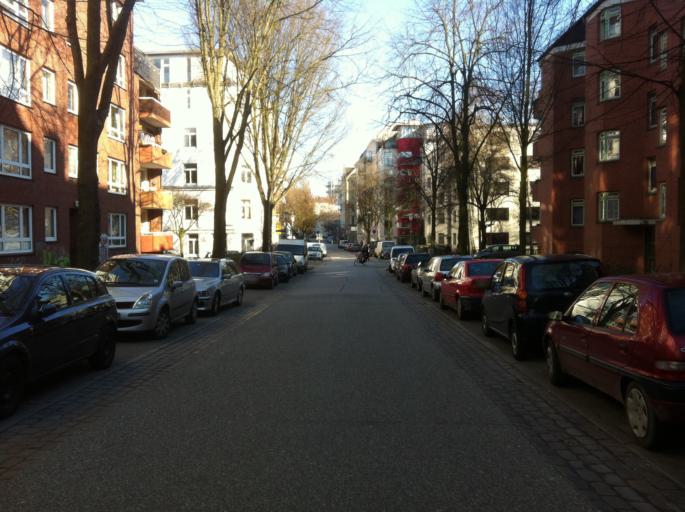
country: DE
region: Hamburg
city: St. Pauli
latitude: 53.5544
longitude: 9.9598
